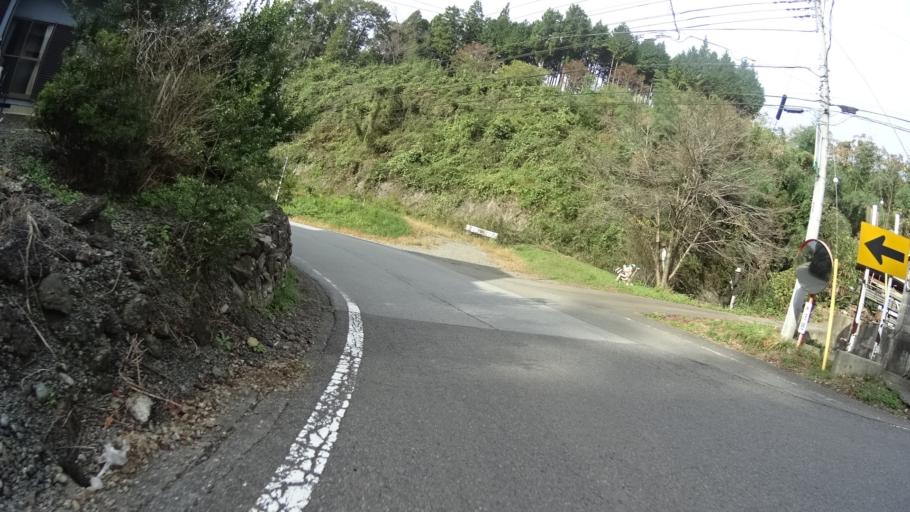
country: JP
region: Yamanashi
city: Otsuki
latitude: 35.6193
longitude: 139.0179
